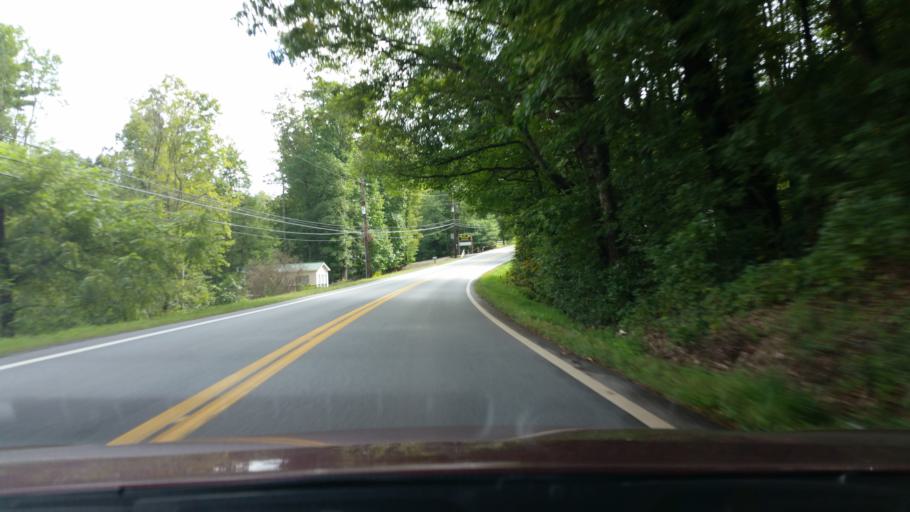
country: US
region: Maryland
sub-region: Washington County
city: Hancock
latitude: 39.6268
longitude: -78.0923
